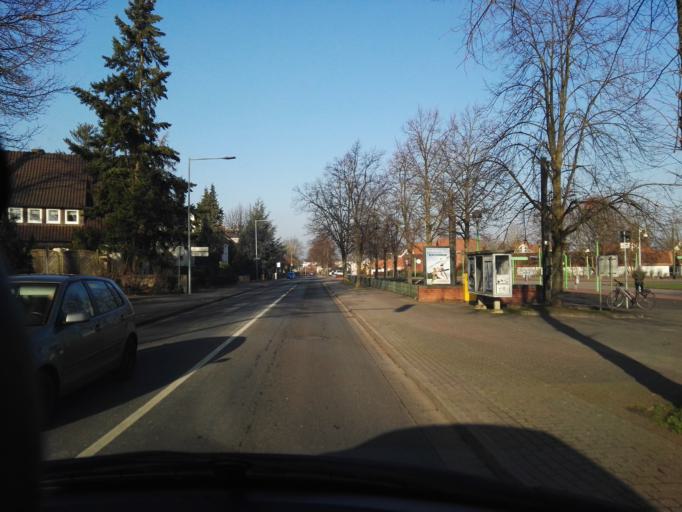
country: DE
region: Lower Saxony
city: Sarstedt
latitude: 52.2354
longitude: 9.8581
